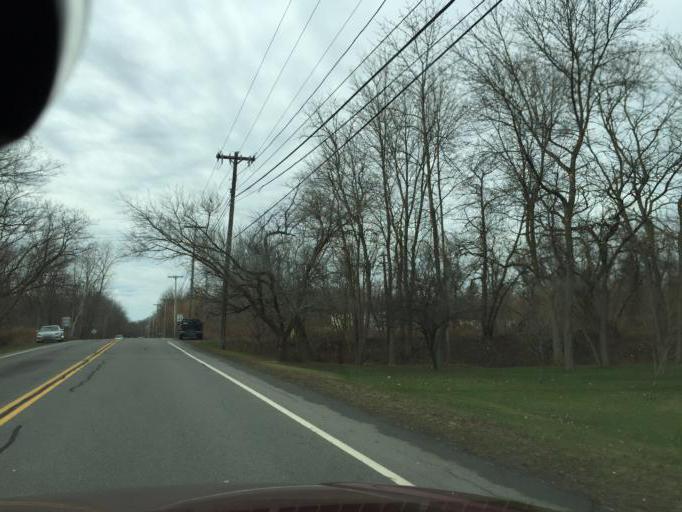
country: US
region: New York
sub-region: Monroe County
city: North Gates
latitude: 43.0935
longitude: -77.6906
